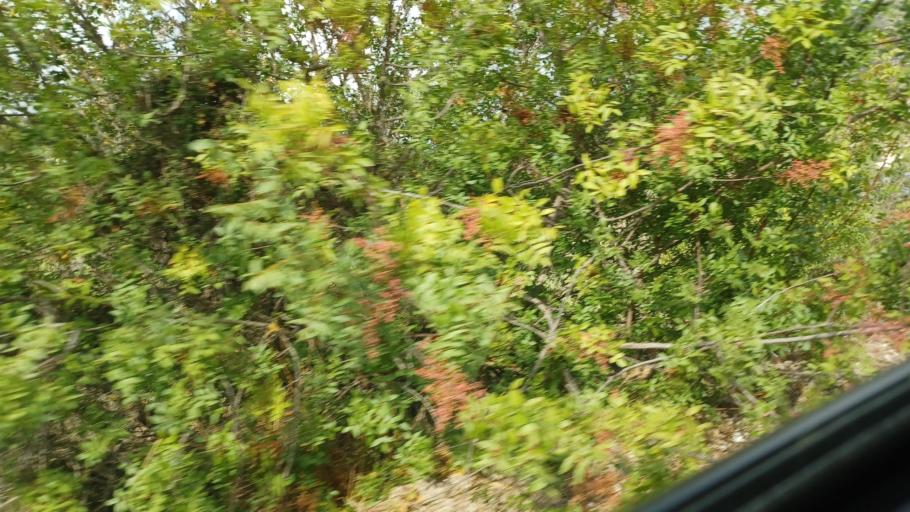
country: CY
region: Pafos
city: Tala
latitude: 34.8735
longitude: 32.4584
